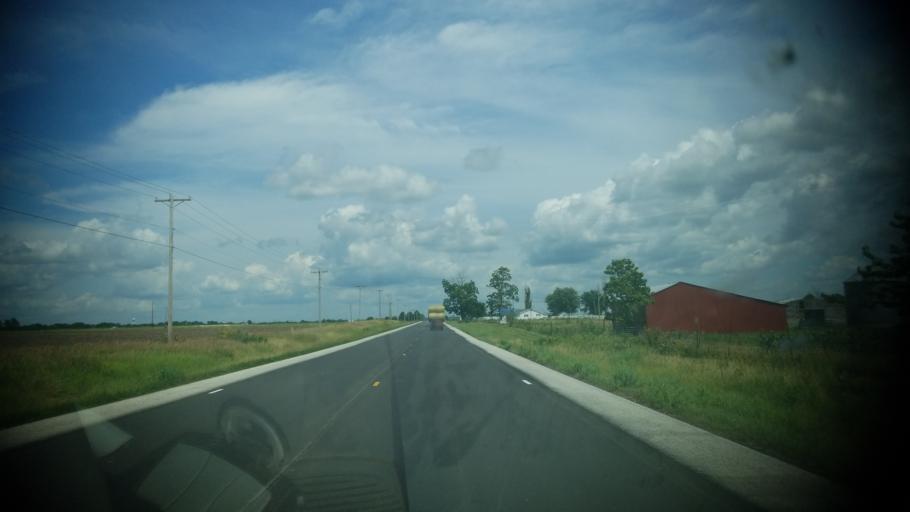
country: US
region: Missouri
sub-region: Pike County
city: Bowling Green
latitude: 39.3444
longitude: -91.2591
